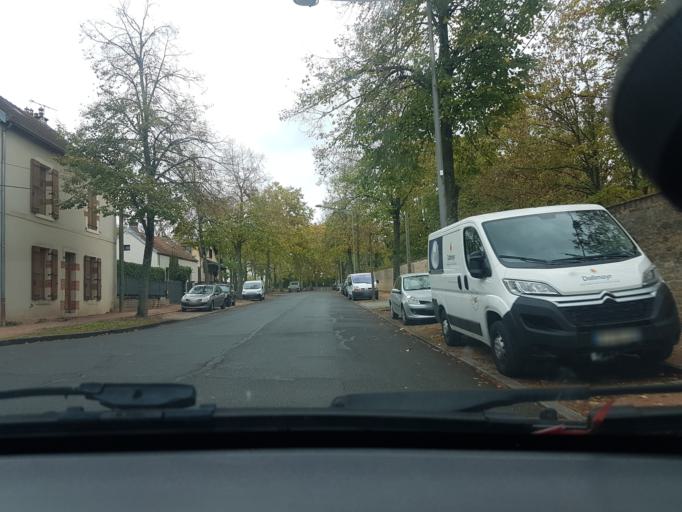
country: FR
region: Bourgogne
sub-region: Departement de la Cote-d'Or
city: Saint-Apollinaire
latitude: 47.3199
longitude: 5.0578
